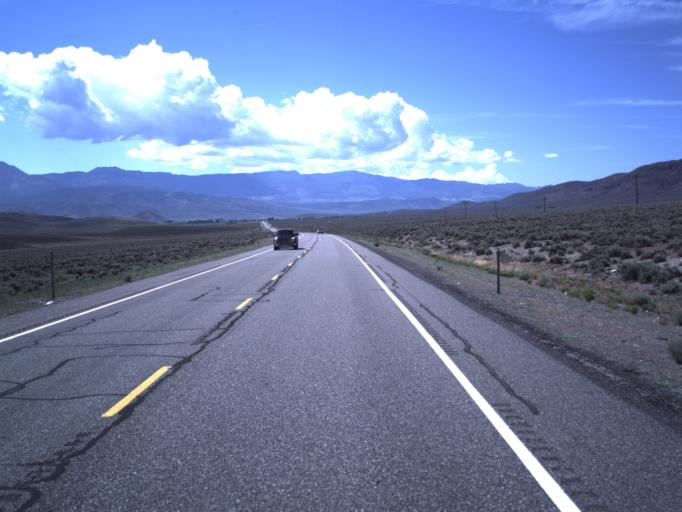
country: US
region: Utah
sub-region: Piute County
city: Junction
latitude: 38.2885
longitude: -112.2253
